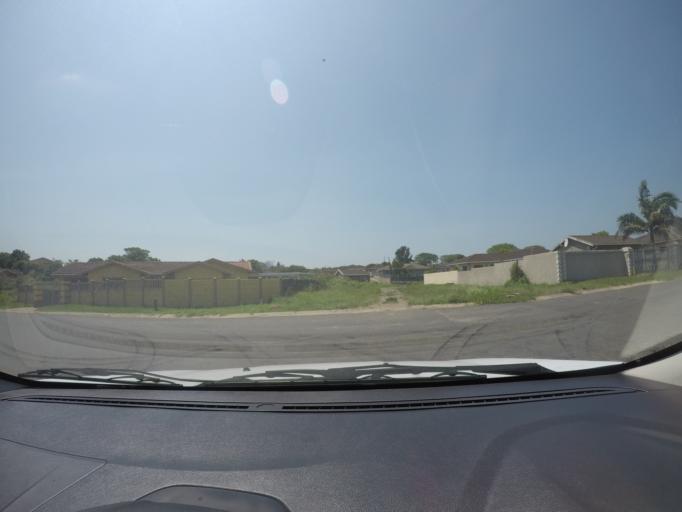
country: ZA
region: KwaZulu-Natal
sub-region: uThungulu District Municipality
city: eSikhawini
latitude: -28.8659
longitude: 31.9206
